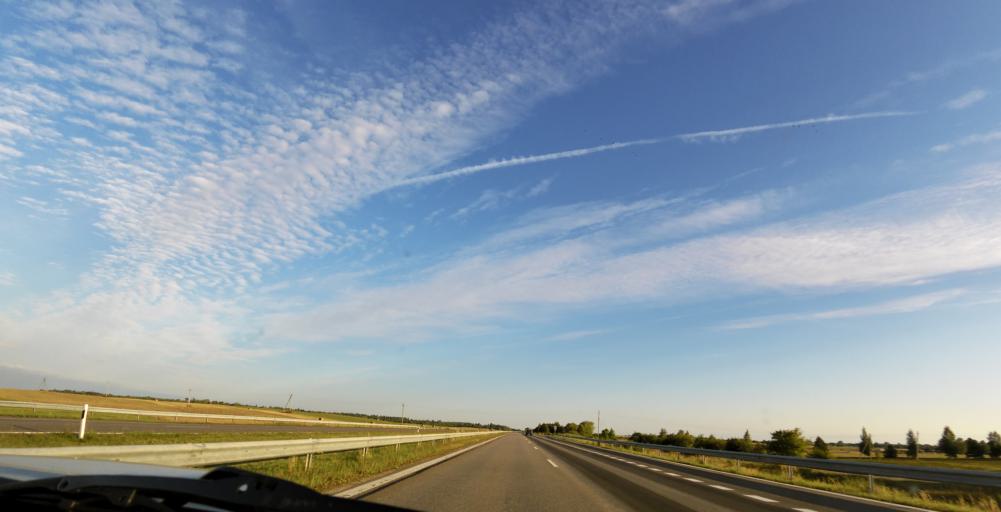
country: LT
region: Vilnius County
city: Ukmerge
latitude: 55.1586
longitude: 24.8205
